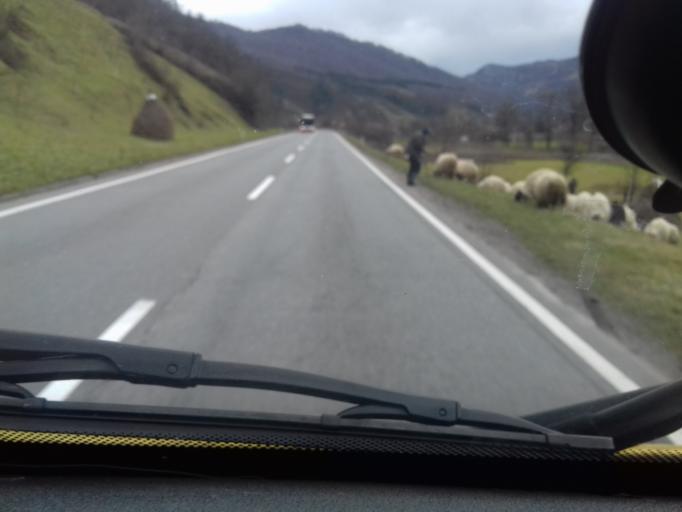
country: BA
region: Federation of Bosnia and Herzegovina
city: Zeljezno Polje
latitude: 44.3421
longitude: 17.9229
